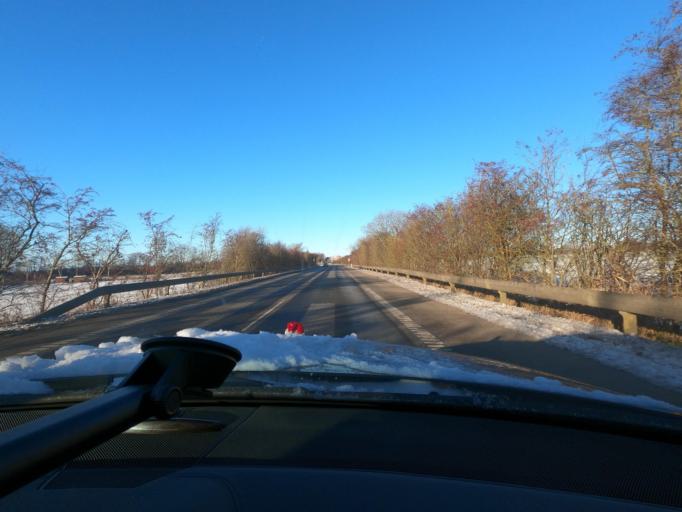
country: DK
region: South Denmark
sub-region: Sonderborg Kommune
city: Horuphav
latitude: 54.8926
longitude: 9.9704
